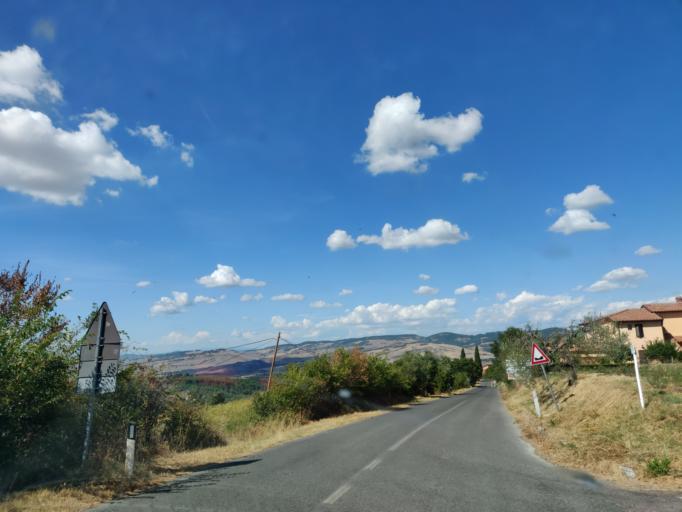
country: IT
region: Tuscany
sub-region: Provincia di Siena
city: Radicofani
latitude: 42.9713
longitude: 11.7364
